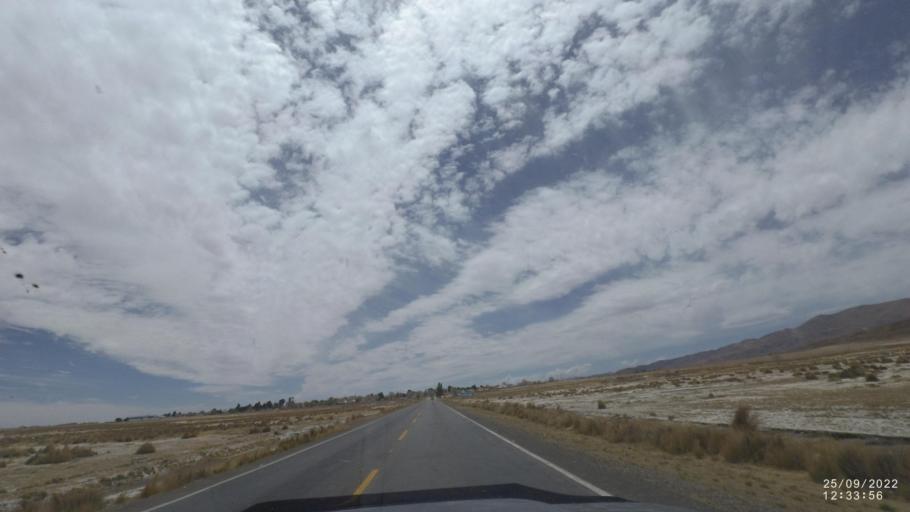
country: BO
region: Oruro
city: Machacamarca
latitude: -18.1842
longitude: -67.0155
